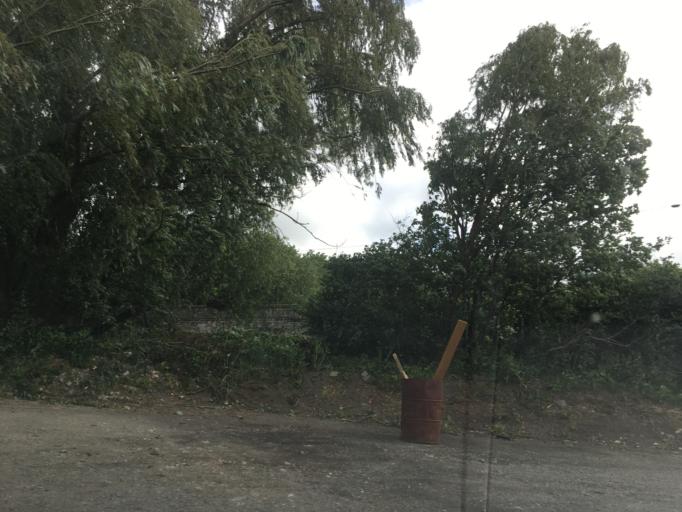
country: GB
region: Scotland
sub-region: Edinburgh
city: Newbridge
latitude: 55.9395
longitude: -3.4114
